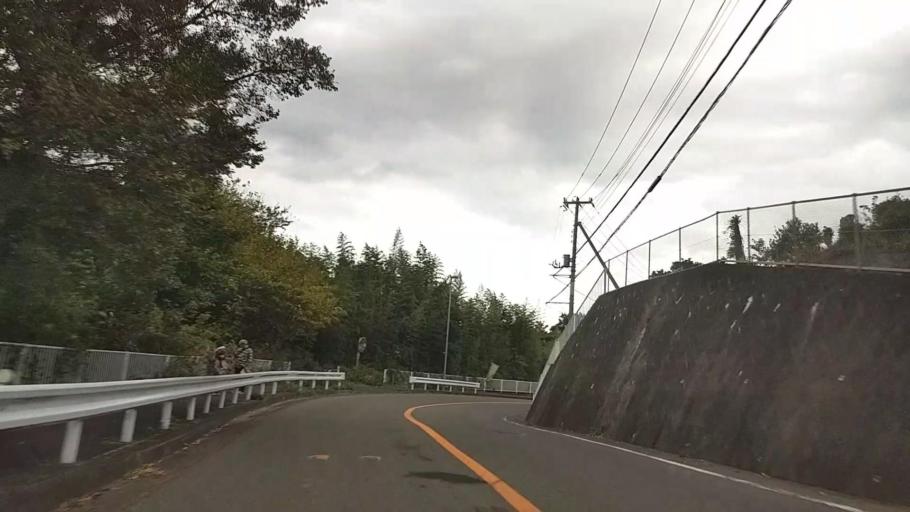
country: JP
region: Kanagawa
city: Yugawara
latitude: 35.1678
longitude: 139.1358
